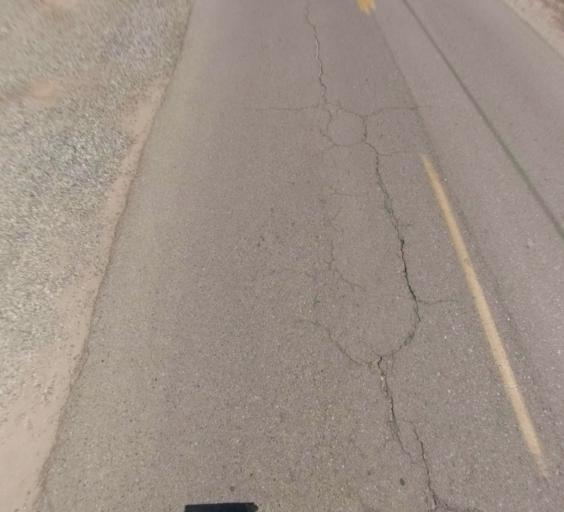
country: US
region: California
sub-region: Madera County
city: Bonadelle Ranchos-Madera Ranchos
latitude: 36.9871
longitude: -119.8794
